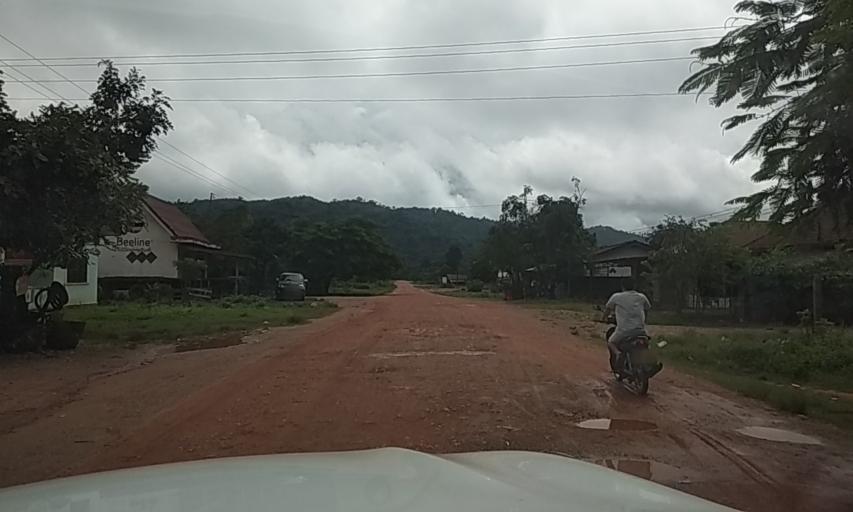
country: LA
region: Bolikhamxai
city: Bolikhan
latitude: 18.5571
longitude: 103.7360
